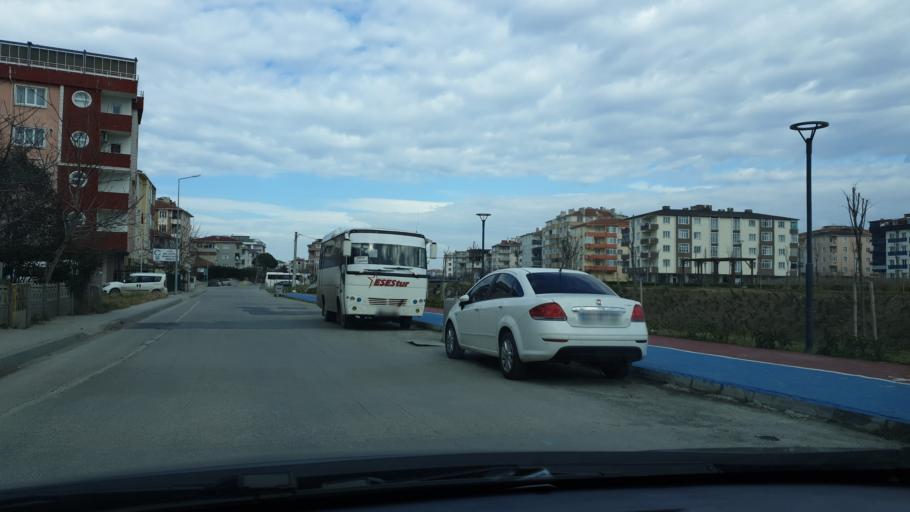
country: TR
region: Tekirdag
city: Cerkezkoey
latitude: 41.2838
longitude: 28.0037
